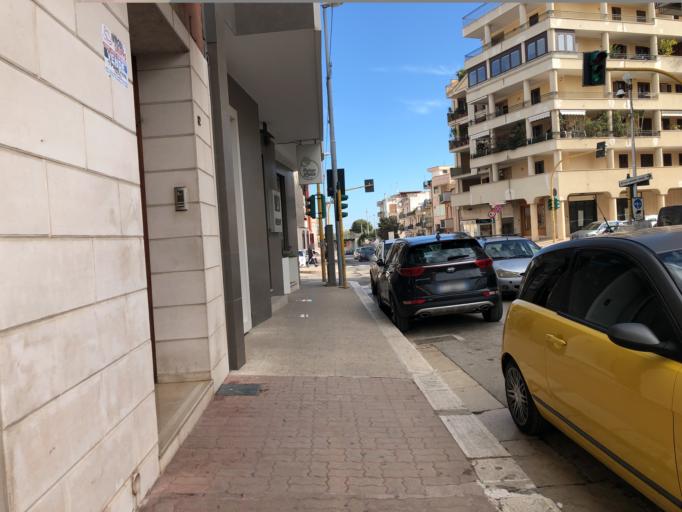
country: IT
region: Apulia
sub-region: Provincia di Barletta - Andria - Trani
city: Andria
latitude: 41.2266
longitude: 16.3101
